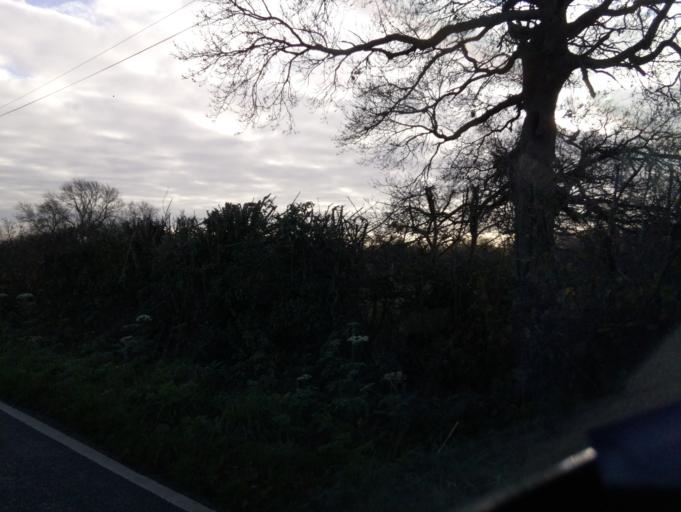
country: GB
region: England
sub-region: Staffordshire
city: Barton under Needwood
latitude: 52.7968
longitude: -1.7112
